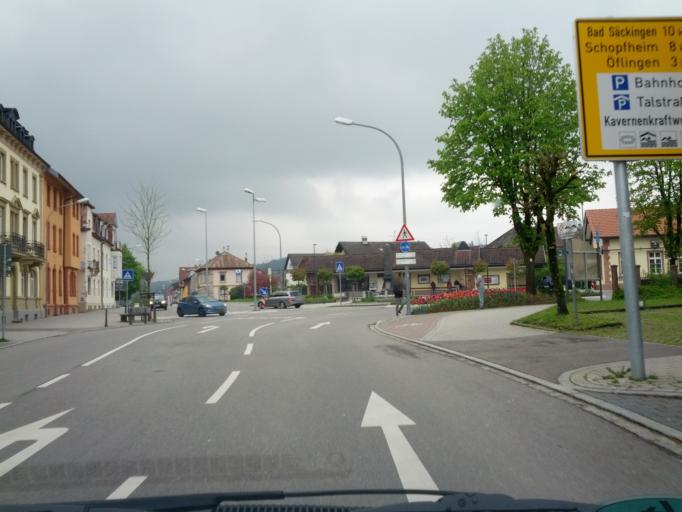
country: DE
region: Baden-Wuerttemberg
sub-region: Freiburg Region
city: Wehr
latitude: 47.6251
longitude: 7.9043
